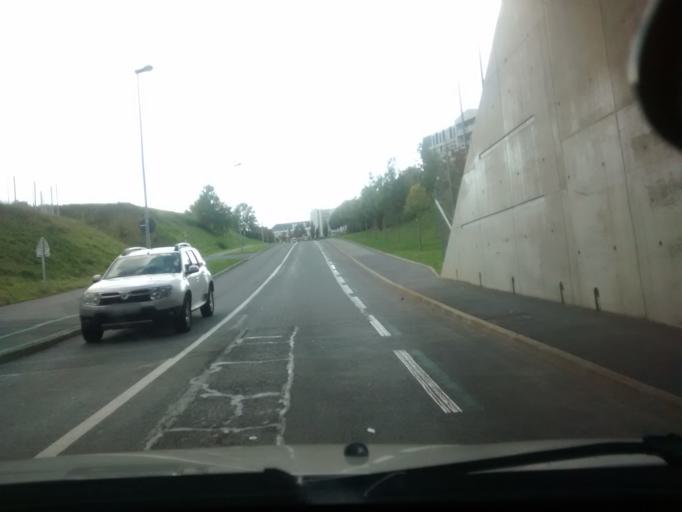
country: FR
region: Brittany
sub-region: Departement d'Ille-et-Vilaine
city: Cesson-Sevigne
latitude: 48.1117
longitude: -1.6085
